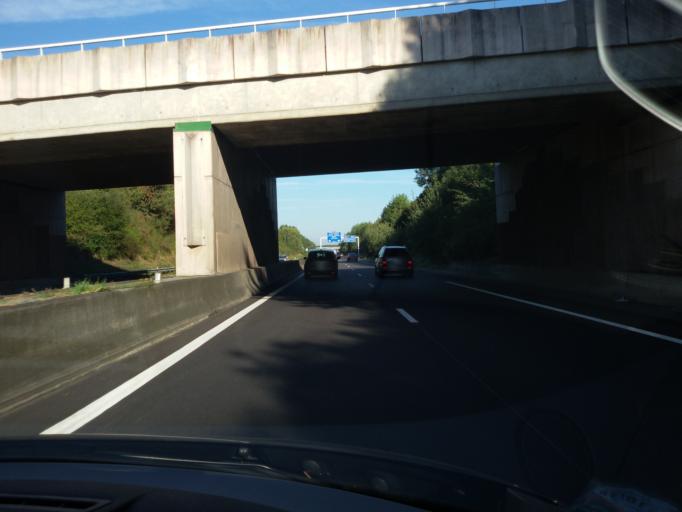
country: FR
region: Centre
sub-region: Departement du Cher
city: Vierzon
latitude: 47.2370
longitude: 2.0882
